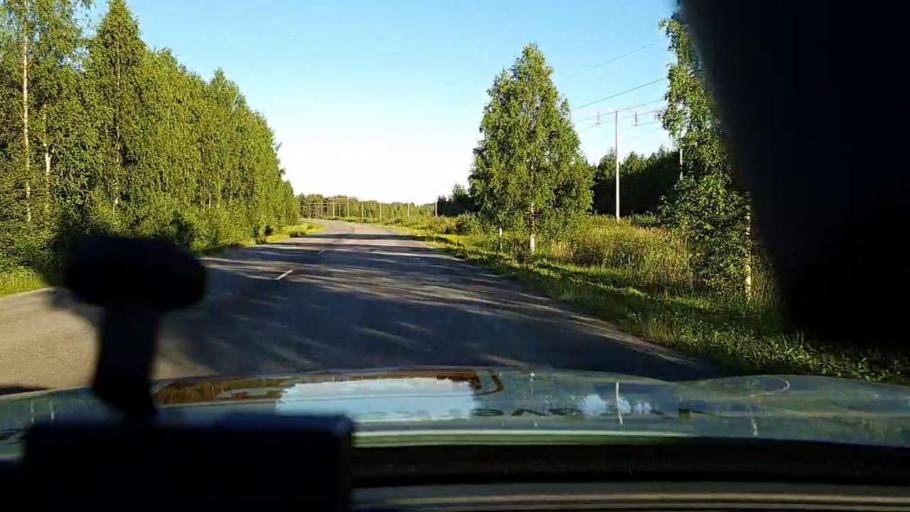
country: SE
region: Norrbotten
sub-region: Lulea Kommun
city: Lulea
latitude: 65.6102
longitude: 22.1652
